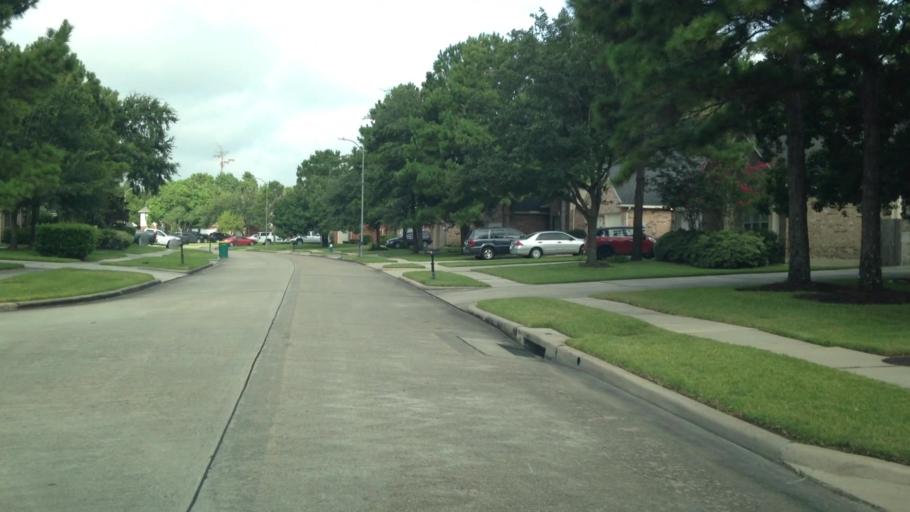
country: US
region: Texas
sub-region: Harris County
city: Atascocita
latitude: 29.9313
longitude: -95.1731
